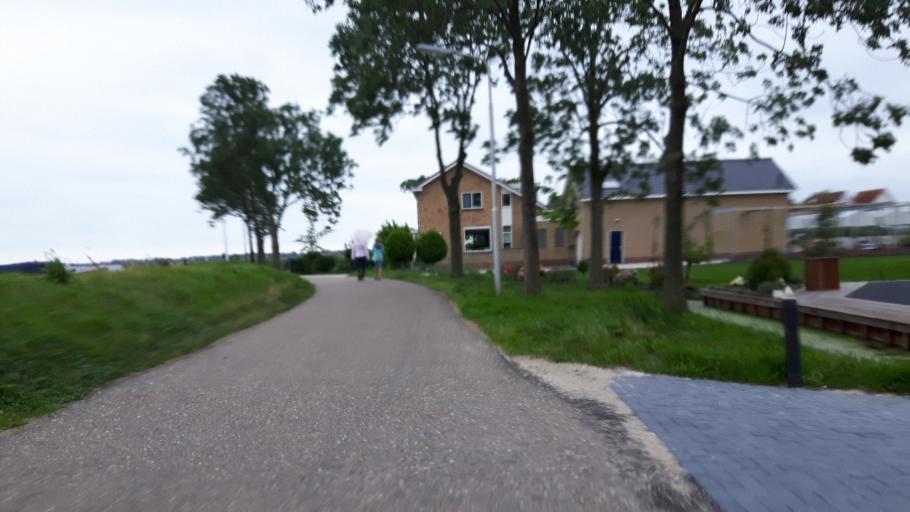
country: NL
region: South Holland
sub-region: Gemeente Kaag en Braassem
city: Oude Wetering
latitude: 52.1990
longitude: 4.6453
